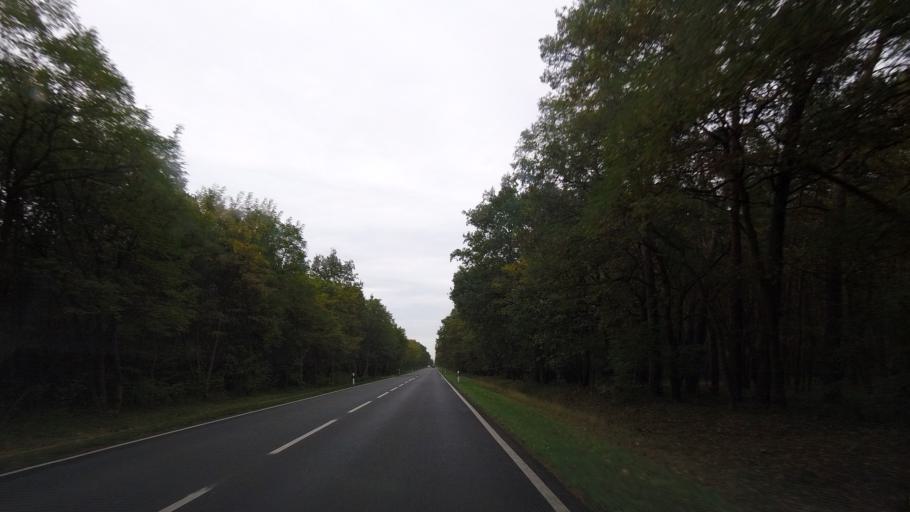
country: DE
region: Brandenburg
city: Treuenbrietzen
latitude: 52.1380
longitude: 12.9126
